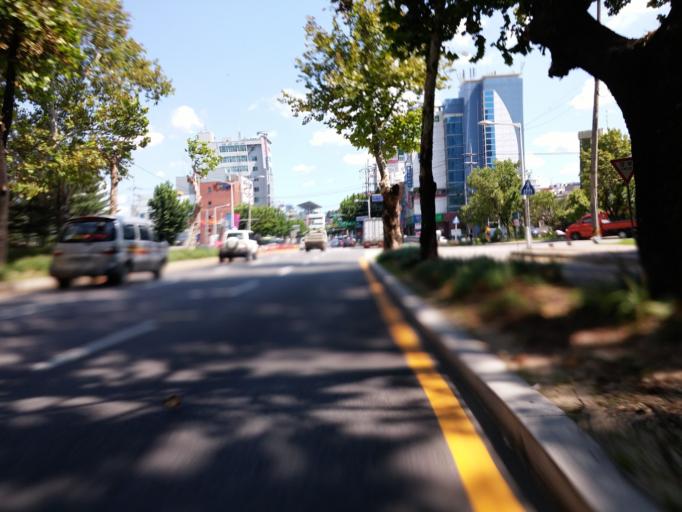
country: KR
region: Chungcheongbuk-do
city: Cheongju-si
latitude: 36.6327
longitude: 127.4379
